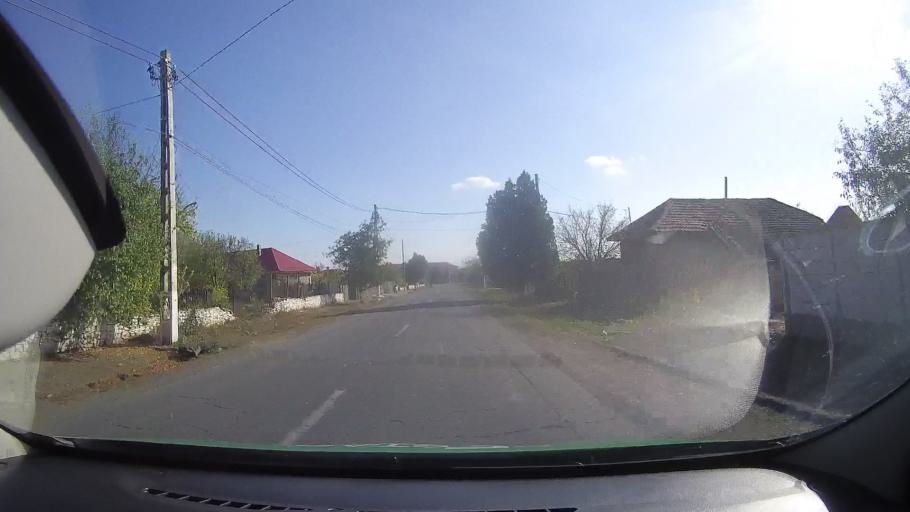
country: RO
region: Constanta
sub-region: Comuna Mihai Viteazu
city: Mihai Viteazu
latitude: 44.6307
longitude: 28.7302
